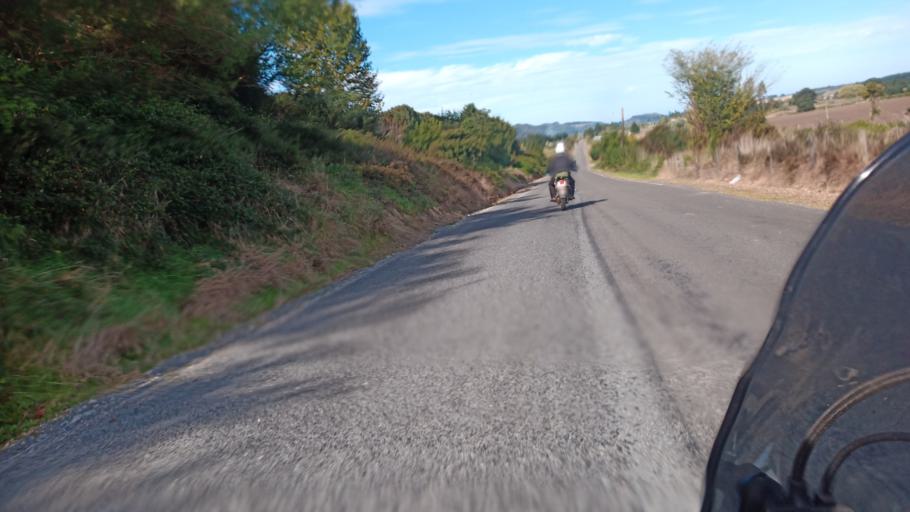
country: NZ
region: Hawke's Bay
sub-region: Wairoa District
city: Wairoa
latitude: -39.0660
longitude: 177.1355
